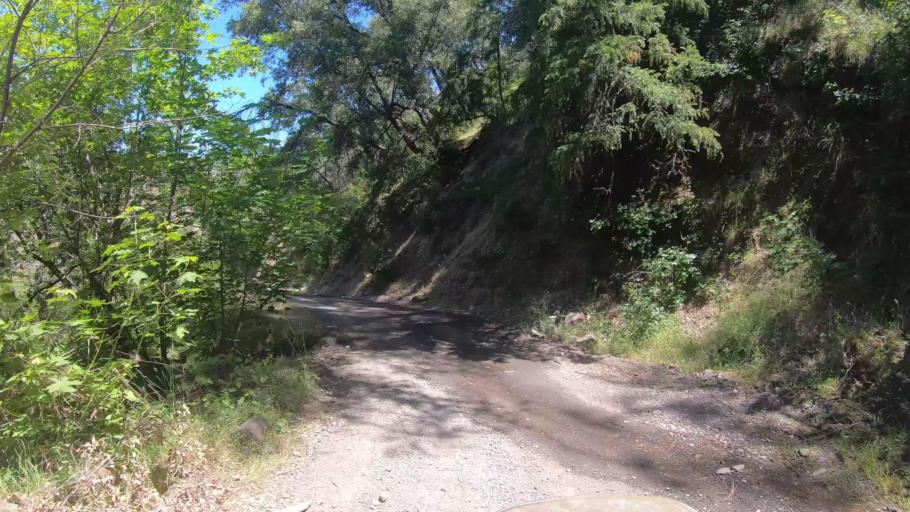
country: US
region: California
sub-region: Tuolumne County
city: Tuolumne City
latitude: 37.8313
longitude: -120.1028
